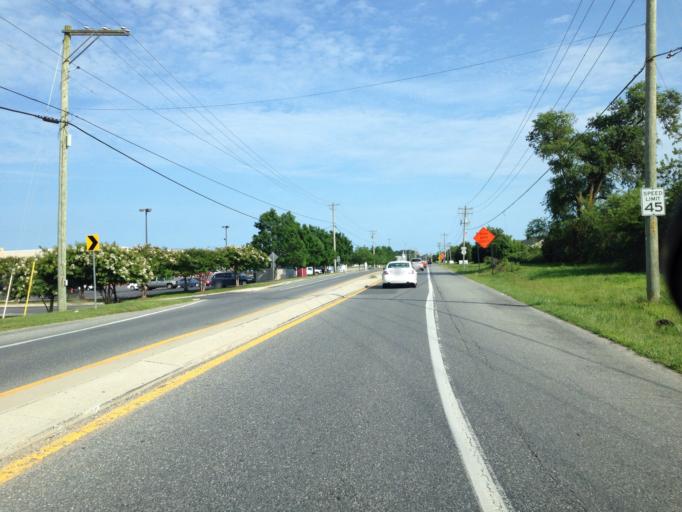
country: US
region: Delaware
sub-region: Sussex County
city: Lewes
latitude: 38.7476
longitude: -75.1738
